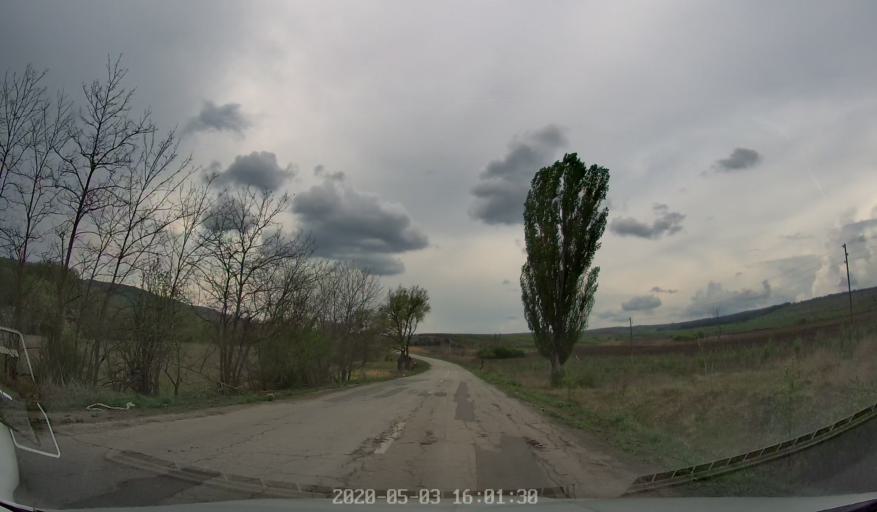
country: MD
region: Stinga Nistrului
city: Bucovat
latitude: 47.1669
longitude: 28.4083
